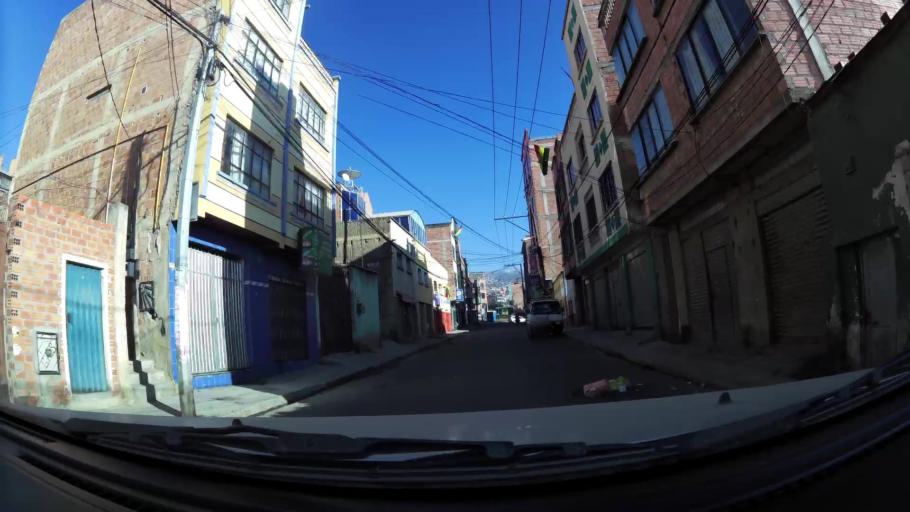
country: BO
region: La Paz
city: La Paz
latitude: -16.5010
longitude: -68.1522
